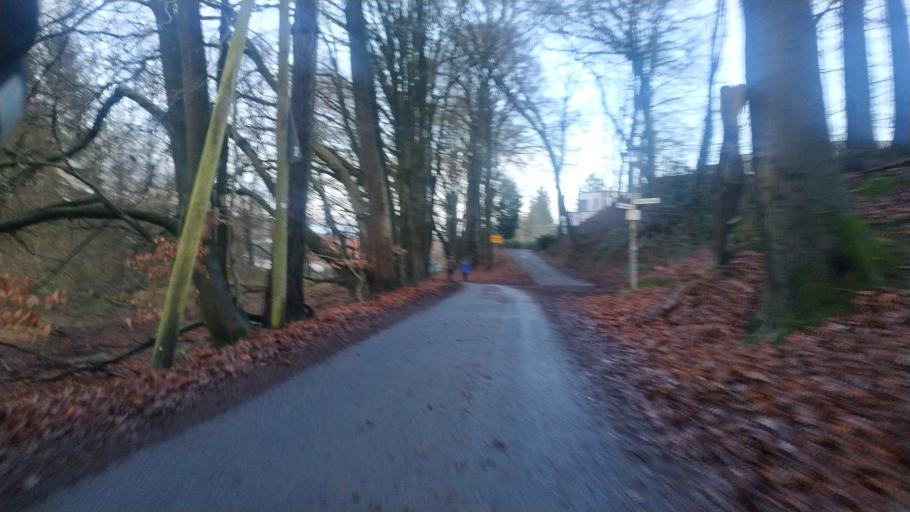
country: DE
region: North Rhine-Westphalia
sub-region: Regierungsbezirk Munster
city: Mettingen
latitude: 52.3110
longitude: 7.7763
